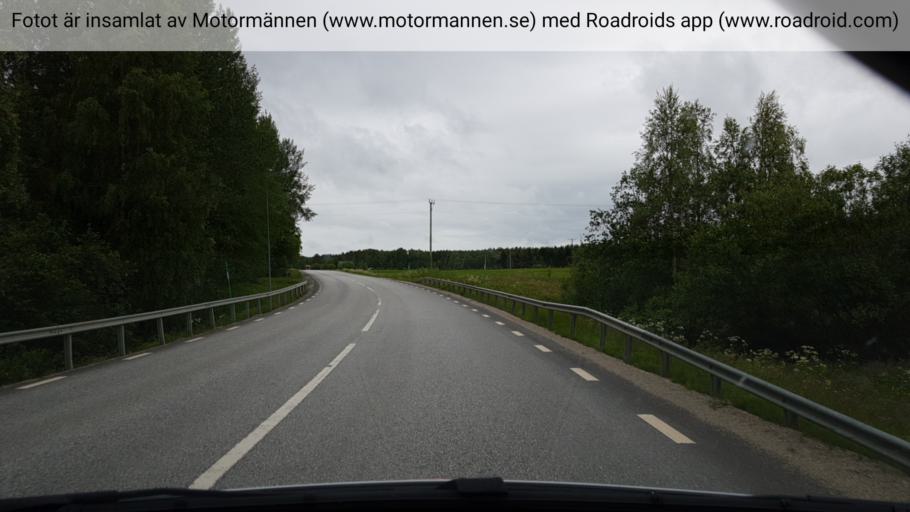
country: SE
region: Vaesterbotten
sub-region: Vindelns Kommun
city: Vindeln
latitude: 64.1227
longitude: 19.5603
